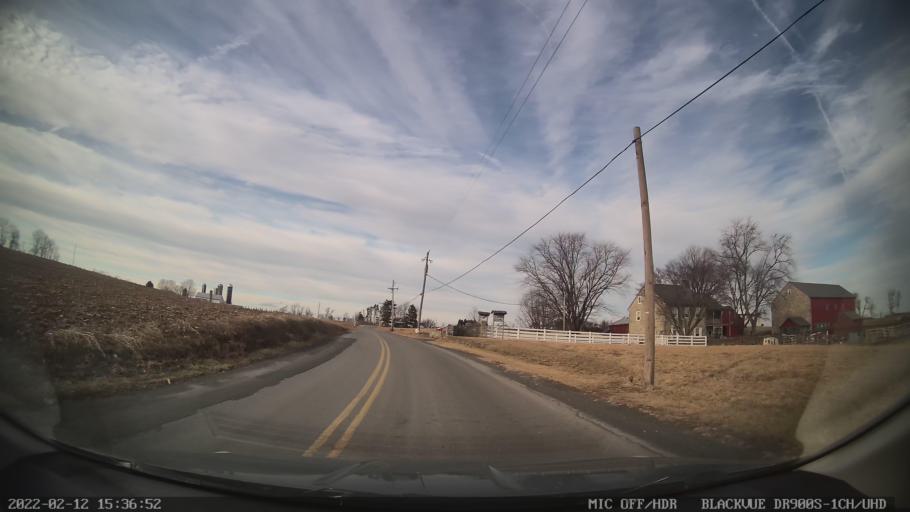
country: US
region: Pennsylvania
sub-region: Berks County
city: Topton
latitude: 40.4948
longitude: -75.7364
